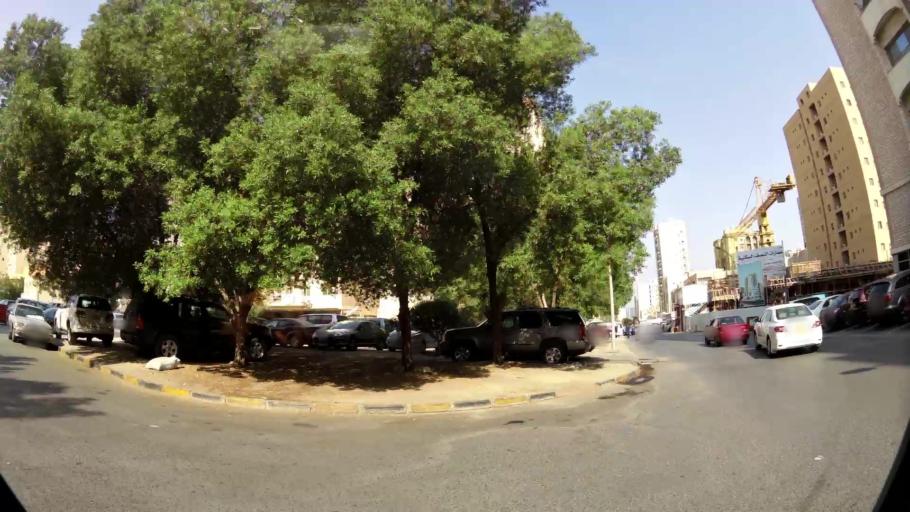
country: KW
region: Muhafazat Hawalli
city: Hawalli
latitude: 29.3321
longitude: 48.0236
